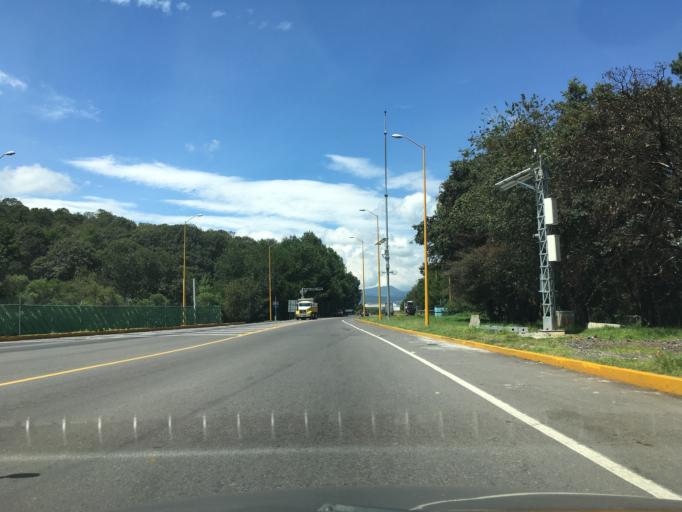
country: MX
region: Michoacan
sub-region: Patzcuaro
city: Santa Ana Chapitiro
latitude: 19.5057
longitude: -101.6596
